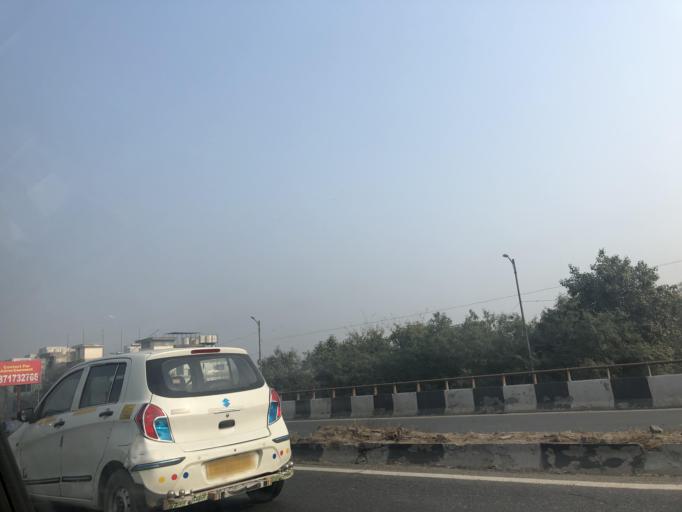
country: IN
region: NCT
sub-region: North West Delhi
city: Pitampura
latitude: 28.6340
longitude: 77.1313
